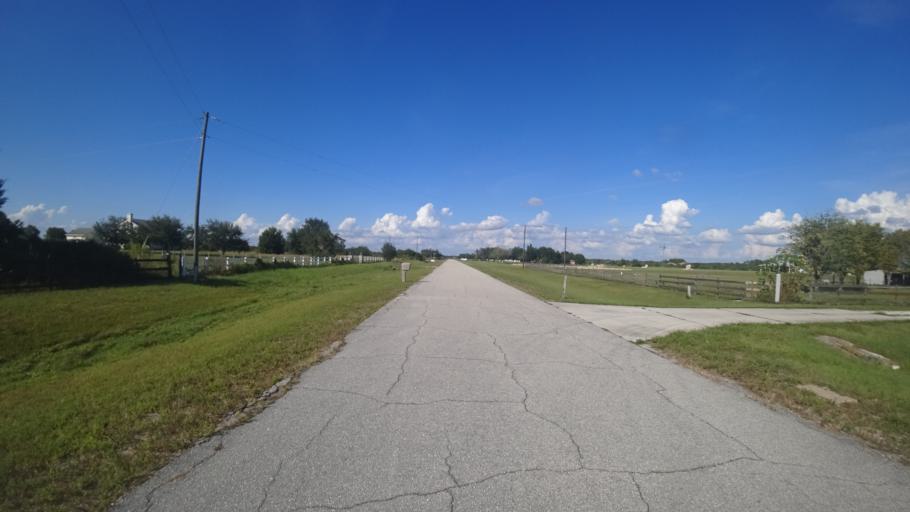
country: US
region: Florida
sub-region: Sarasota County
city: The Meadows
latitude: 27.4184
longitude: -82.2832
